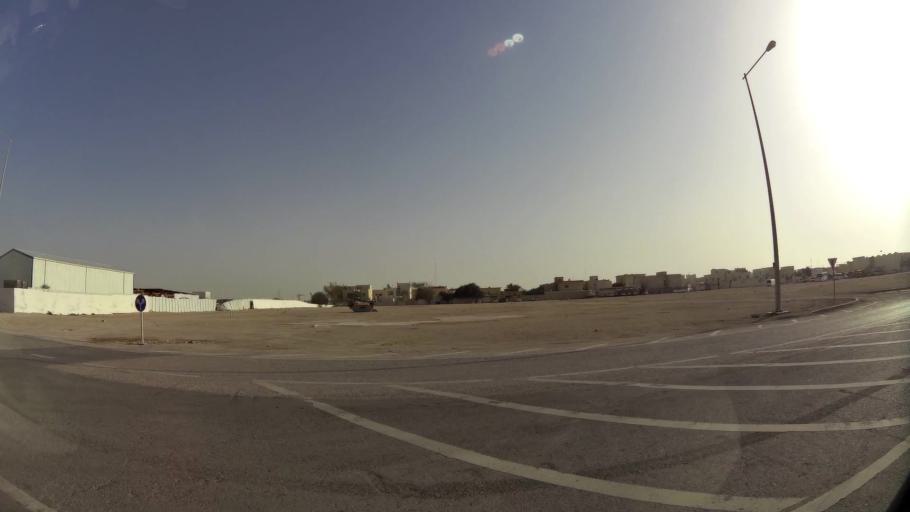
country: QA
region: Baladiyat ar Rayyan
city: Ar Rayyan
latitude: 25.3325
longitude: 51.4304
